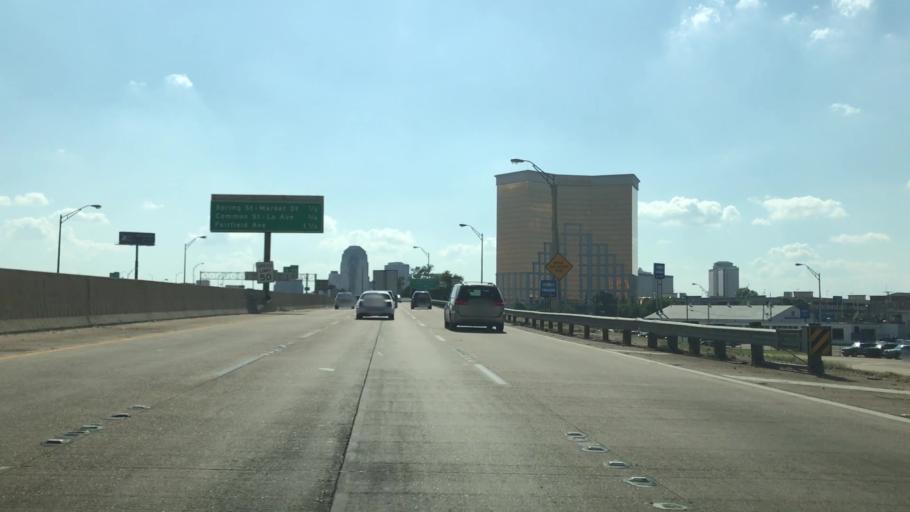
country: US
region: Louisiana
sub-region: Bossier Parish
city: Bossier City
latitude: 32.5141
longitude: -93.7324
